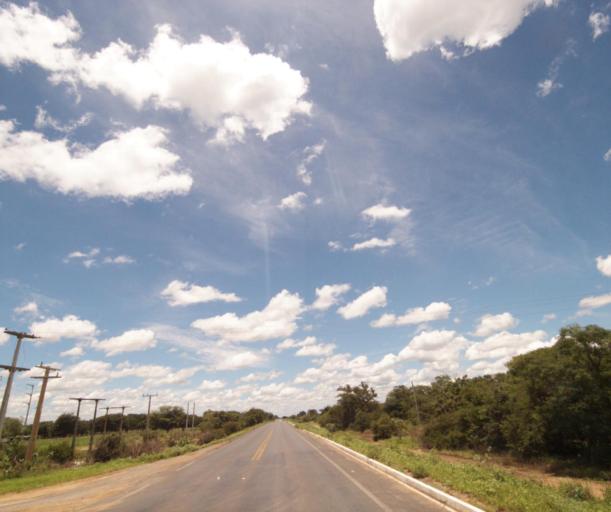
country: BR
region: Bahia
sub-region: Bom Jesus Da Lapa
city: Bom Jesus da Lapa
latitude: -13.2602
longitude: -43.5027
